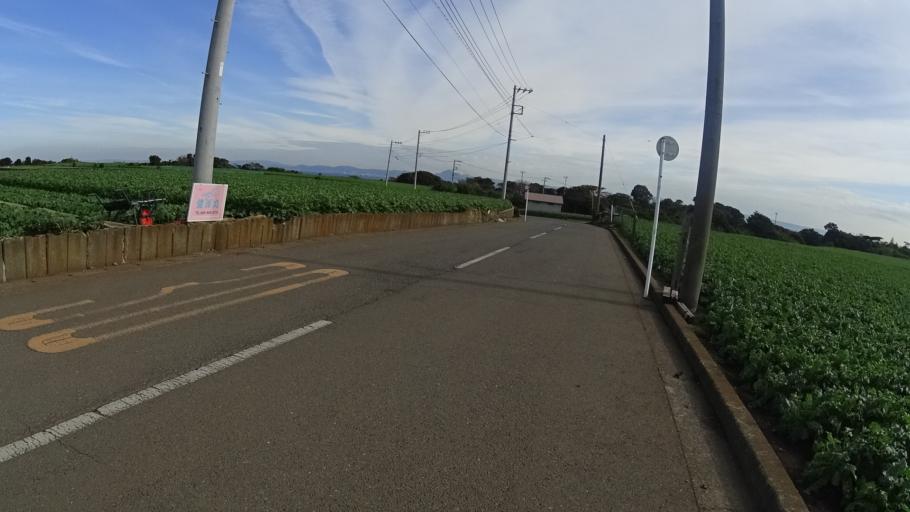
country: JP
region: Kanagawa
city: Miura
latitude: 35.1493
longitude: 139.6753
